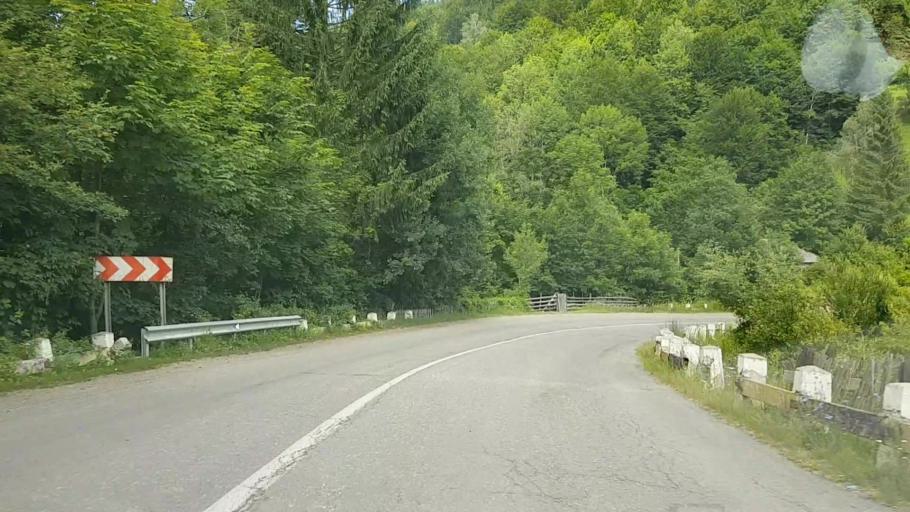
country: RO
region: Neamt
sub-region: Comuna Pangarati
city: Pangarati
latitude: 46.9907
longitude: 26.1196
